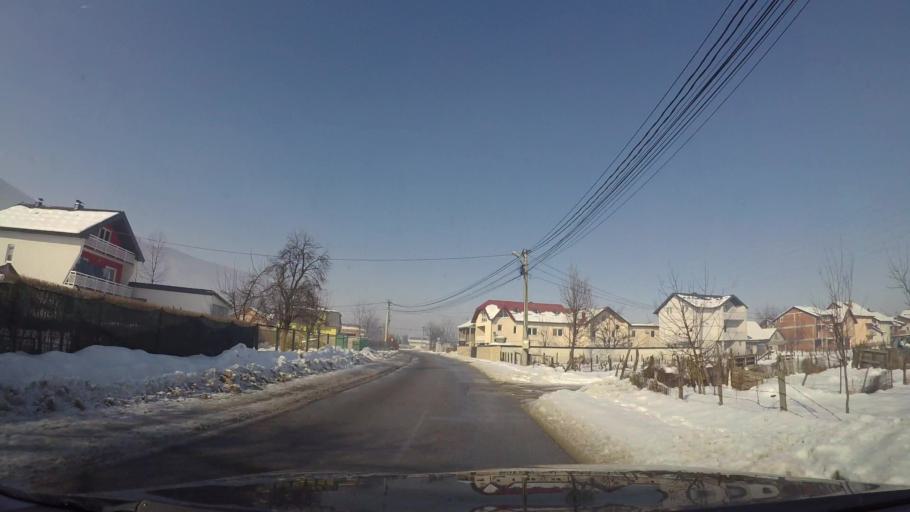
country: BA
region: Federation of Bosnia and Herzegovina
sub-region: Kanton Sarajevo
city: Sarajevo
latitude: 43.8076
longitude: 18.3003
